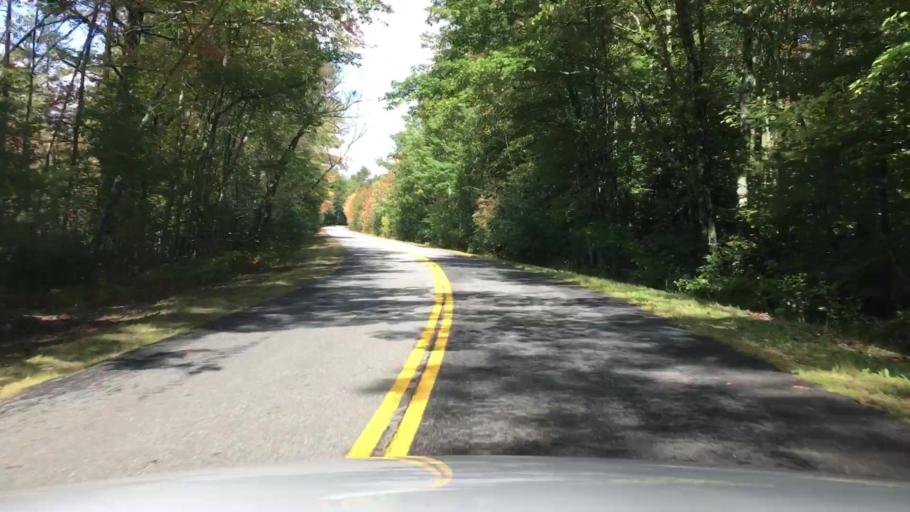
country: US
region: Maine
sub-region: Sagadahoc County
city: North Bath
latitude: 43.9534
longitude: -69.8942
